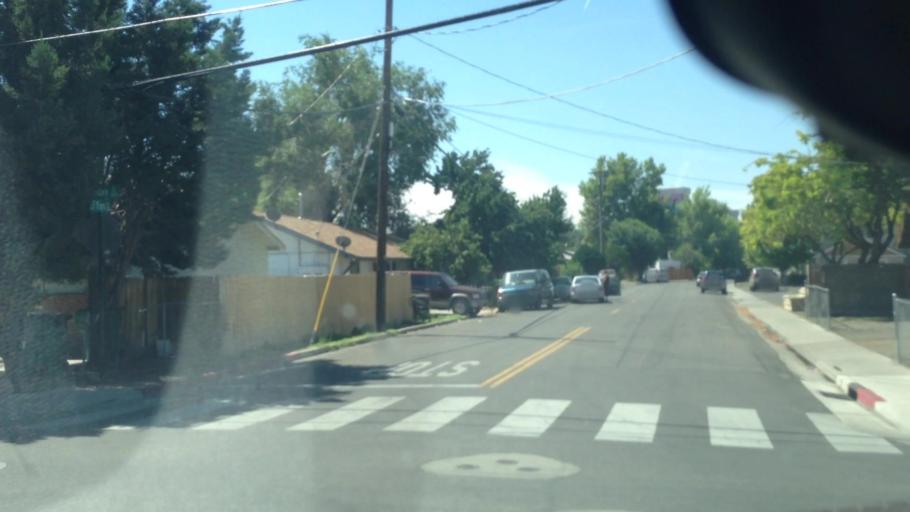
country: US
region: Nevada
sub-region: Washoe County
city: Reno
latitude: 39.4997
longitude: -119.7935
